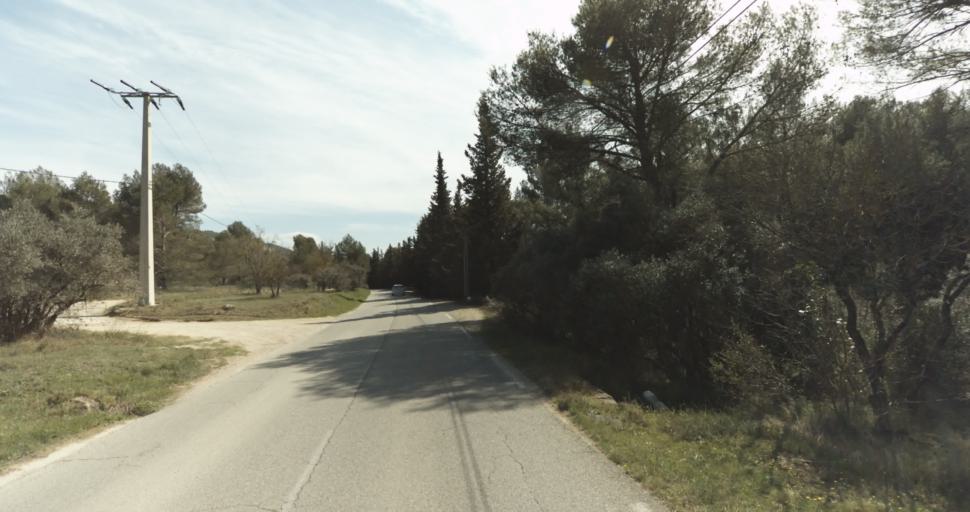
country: FR
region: Provence-Alpes-Cote d'Azur
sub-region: Departement des Bouches-du-Rhone
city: Ventabren
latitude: 43.5284
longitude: 5.2857
